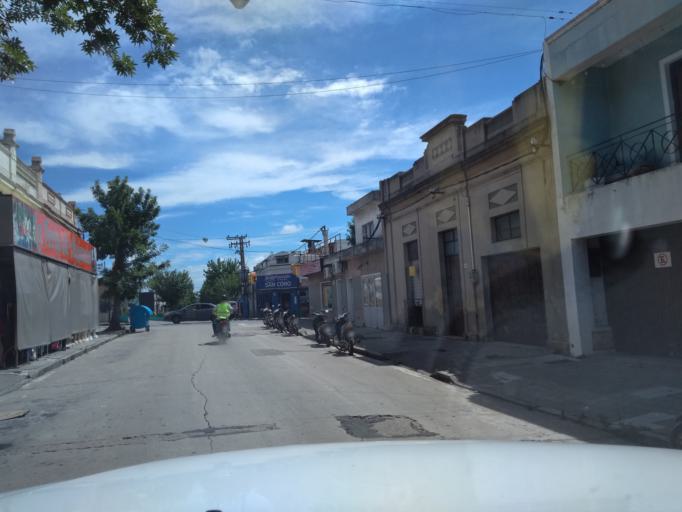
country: UY
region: Florida
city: Florida
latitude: -34.1001
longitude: -56.2162
